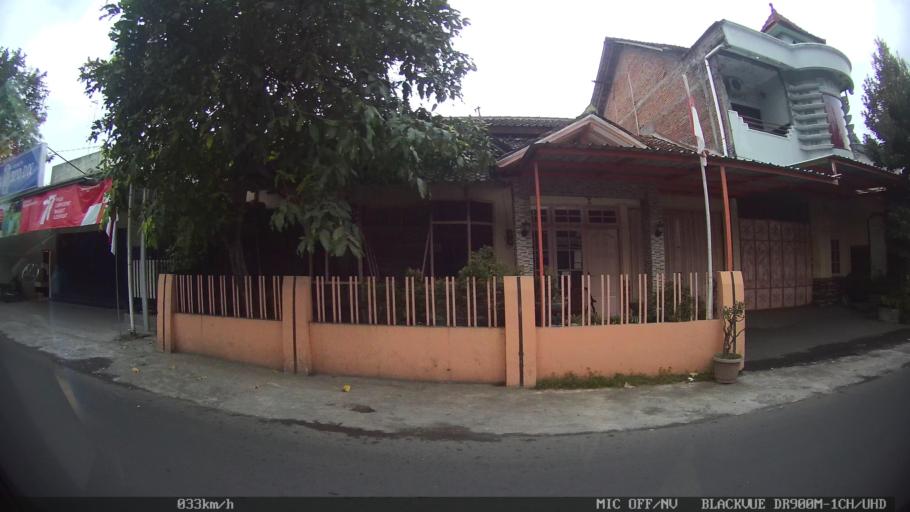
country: ID
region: Daerah Istimewa Yogyakarta
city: Depok
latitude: -7.8301
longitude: 110.4130
